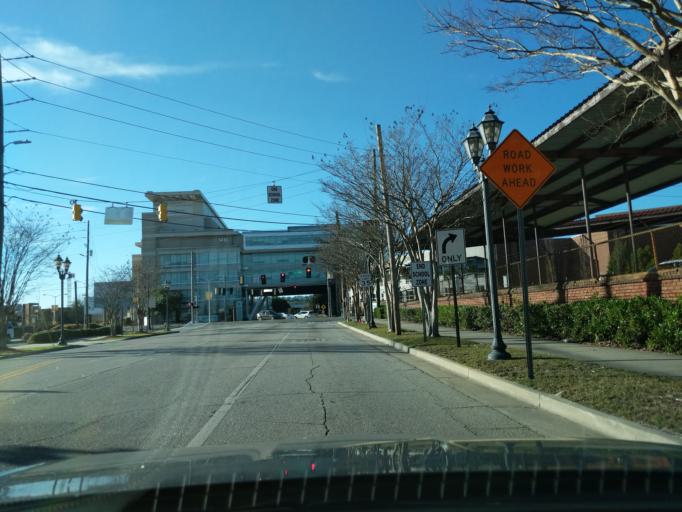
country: US
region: Georgia
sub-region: Richmond County
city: Augusta
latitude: 33.4676
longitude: -81.9846
